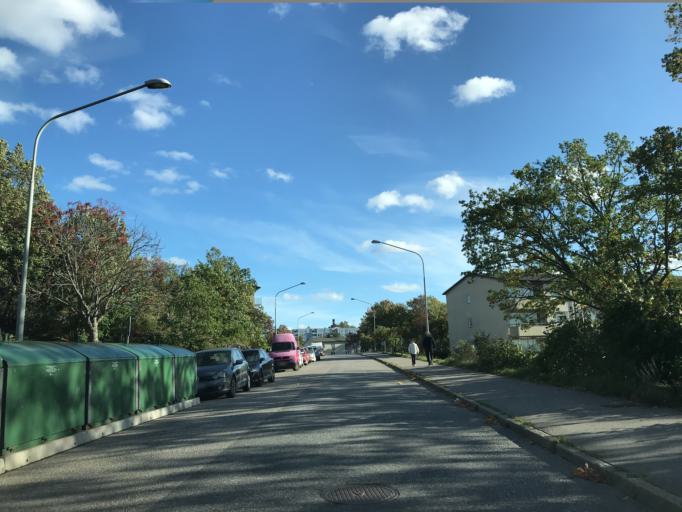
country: SE
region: Stockholm
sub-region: Huddinge Kommun
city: Segeltorp
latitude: 59.2875
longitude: 17.9131
